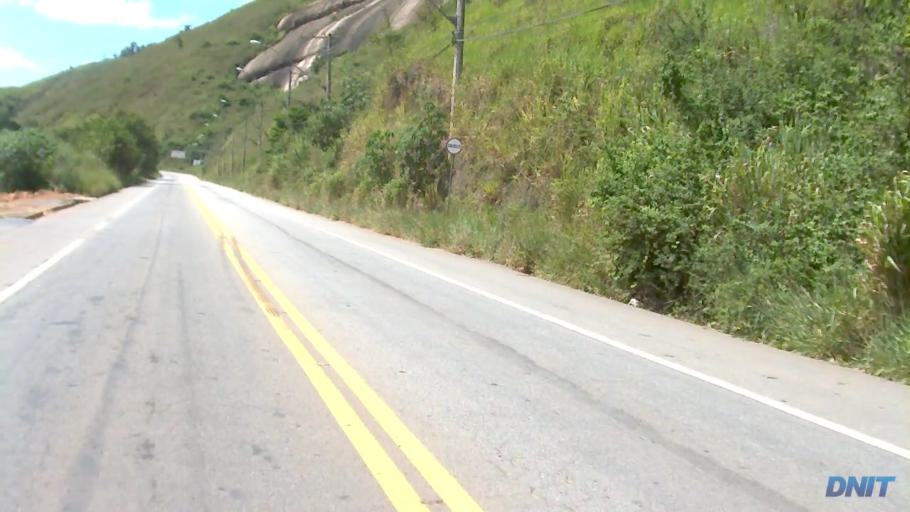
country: BR
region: Minas Gerais
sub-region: Timoteo
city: Timoteo
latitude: -19.5441
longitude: -42.6765
